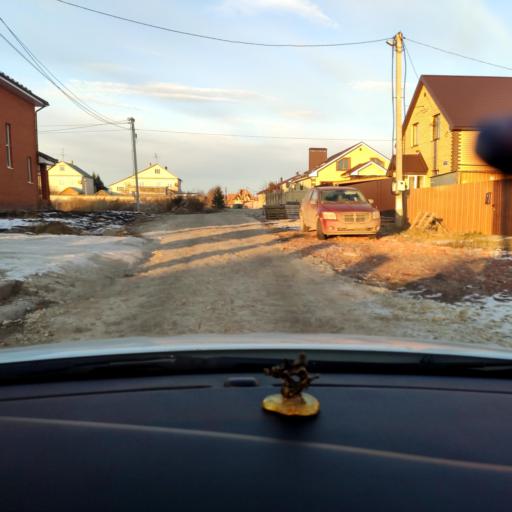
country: RU
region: Tatarstan
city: Stolbishchi
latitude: 55.6049
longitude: 49.1408
